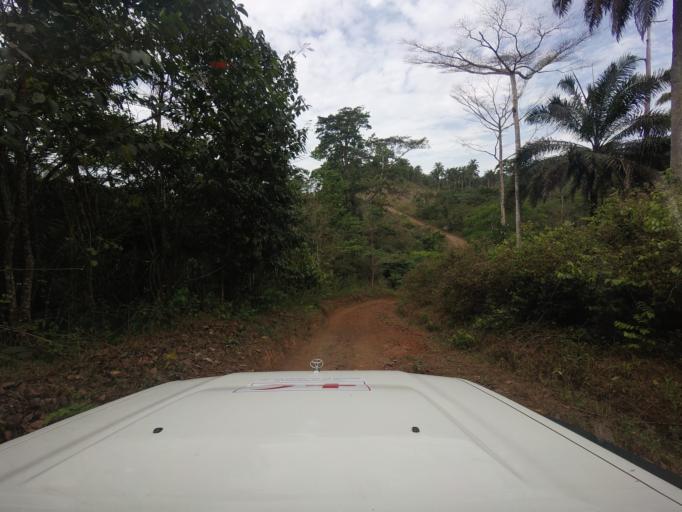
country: SL
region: Eastern Province
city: Buedu
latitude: 8.2463
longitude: -10.2572
